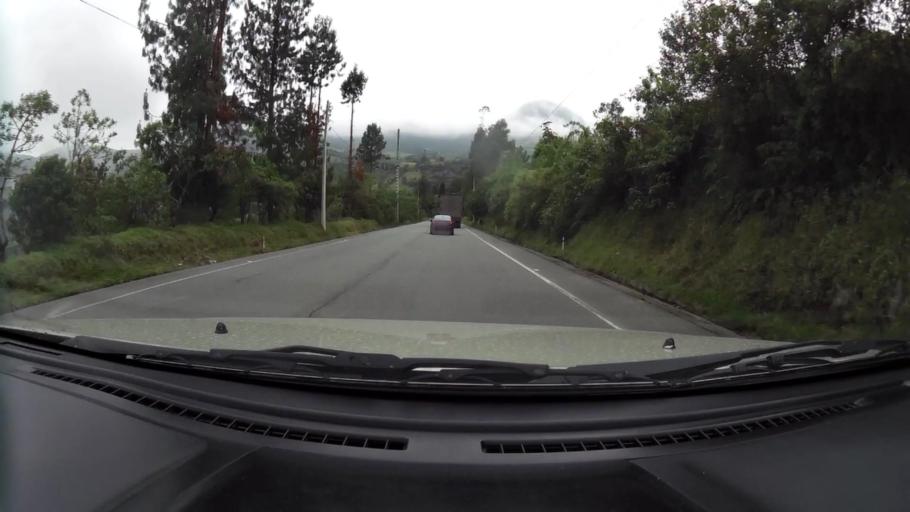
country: EC
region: Canar
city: Canar
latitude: -2.3843
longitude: -78.9709
